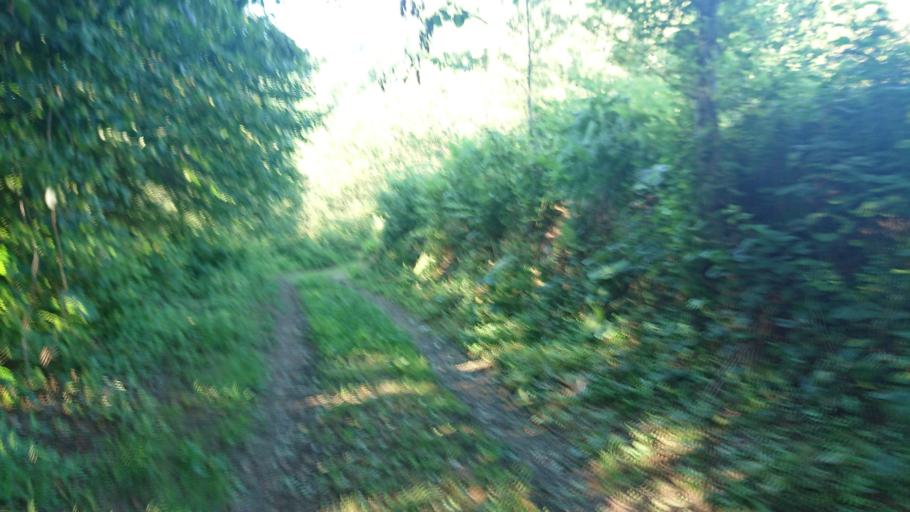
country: TR
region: Rize
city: Rize
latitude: 40.9751
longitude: 40.4981
